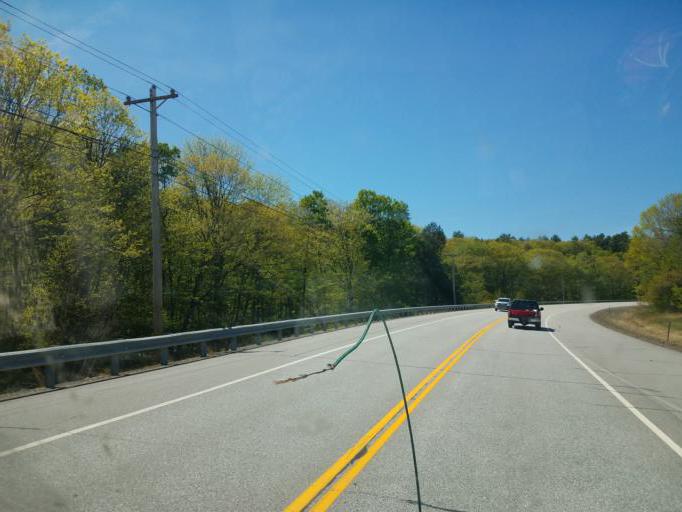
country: US
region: New Hampshire
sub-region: Grafton County
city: Rumney
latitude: 43.8032
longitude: -71.8569
